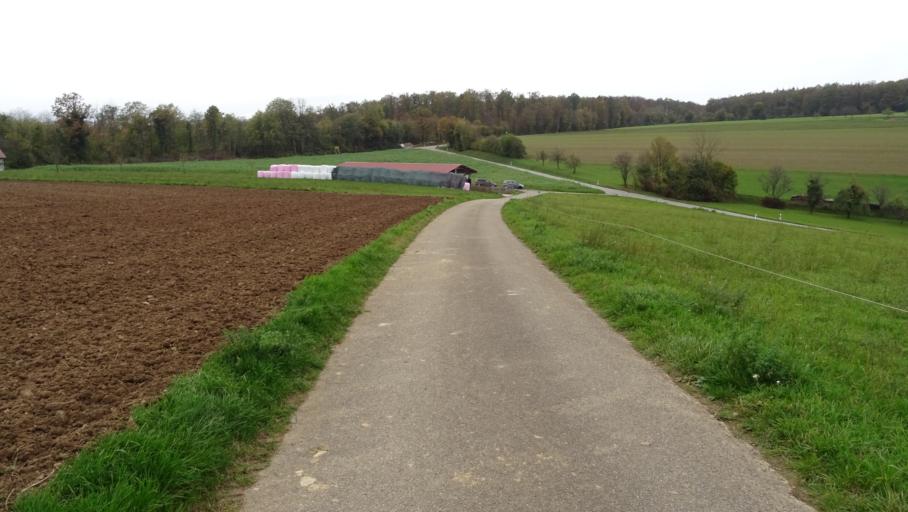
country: DE
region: Baden-Wuerttemberg
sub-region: Karlsruhe Region
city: Obrigheim
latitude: 49.3714
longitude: 9.1157
